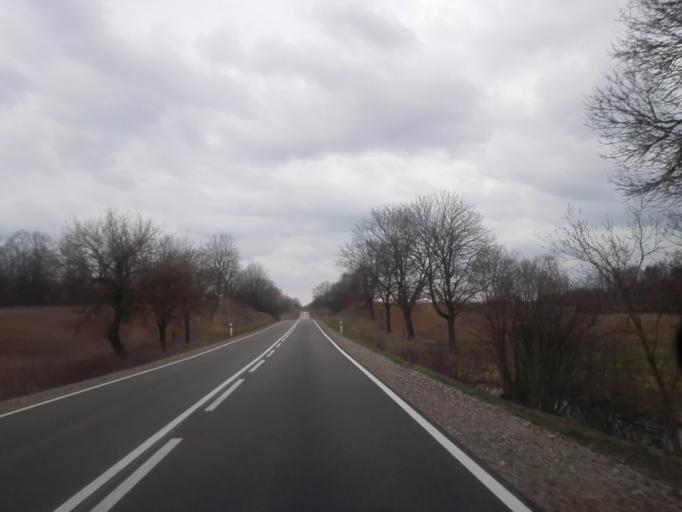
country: PL
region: Podlasie
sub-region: Powiat sejnenski
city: Sejny
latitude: 54.0600
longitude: 23.3571
